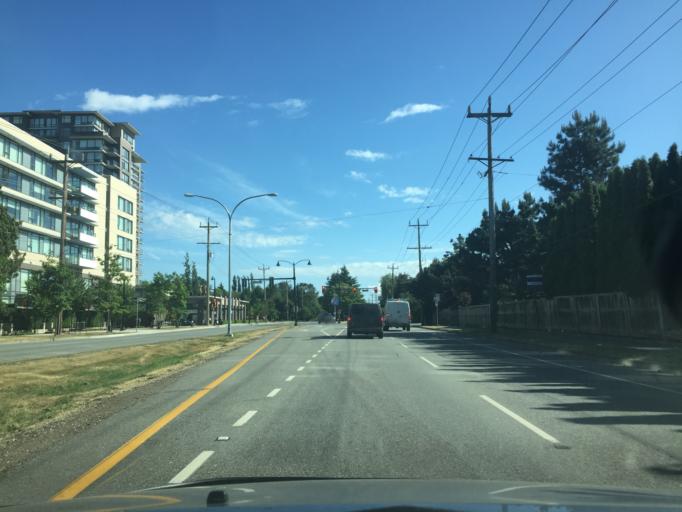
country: CA
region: British Columbia
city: Richmond
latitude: 49.1675
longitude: -123.1247
